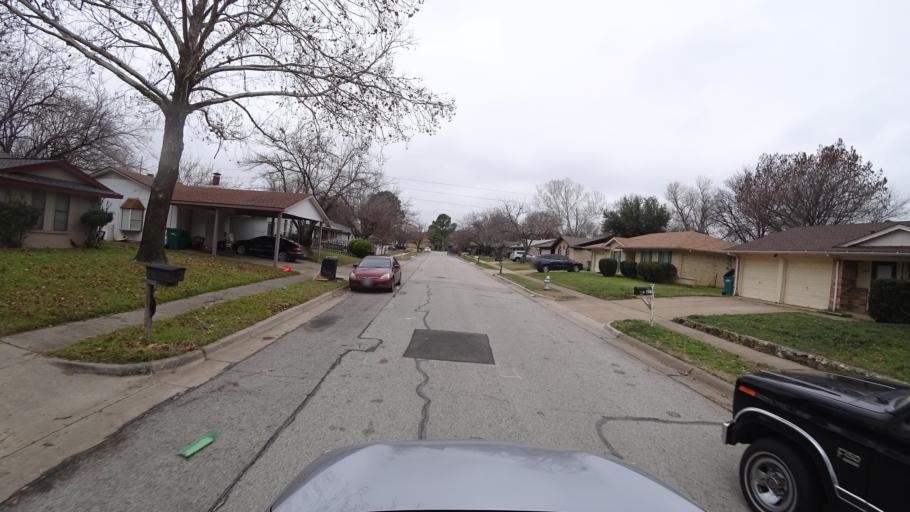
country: US
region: Texas
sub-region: Denton County
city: Lewisville
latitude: 33.0613
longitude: -97.0080
